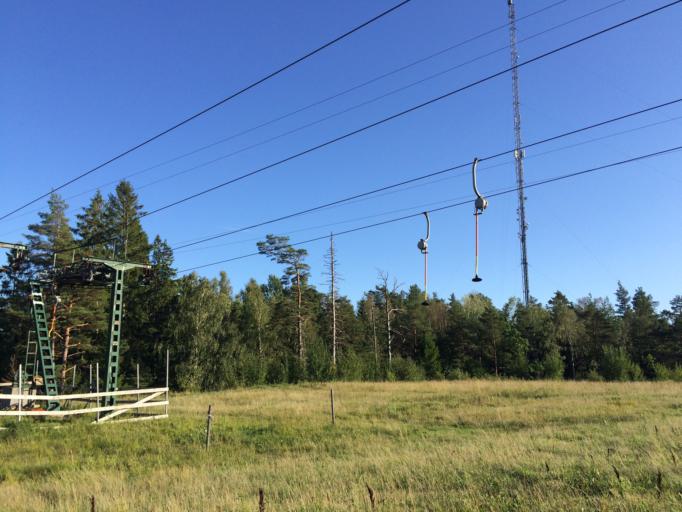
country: SE
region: Vaestra Goetaland
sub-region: Ale Kommun
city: Alafors
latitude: 57.9288
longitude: 12.0915
